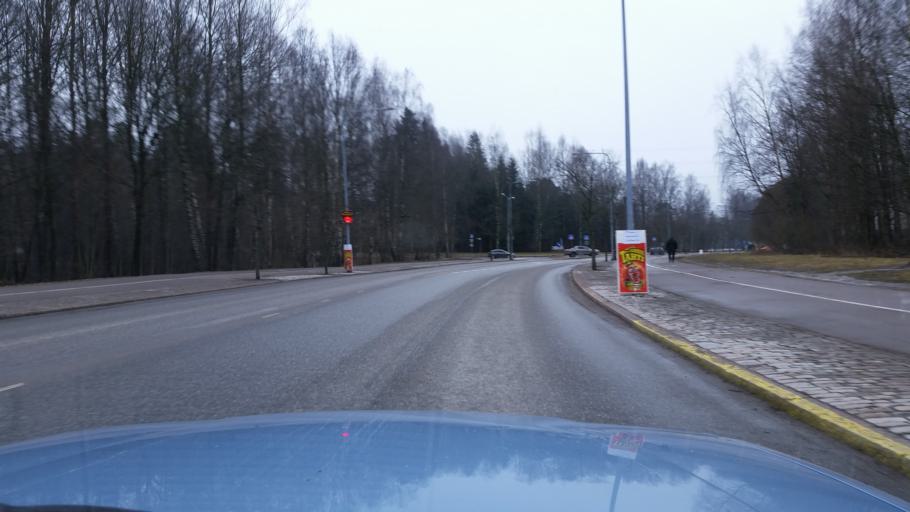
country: FI
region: Uusimaa
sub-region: Helsinki
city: Helsinki
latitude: 60.2260
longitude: 24.9681
